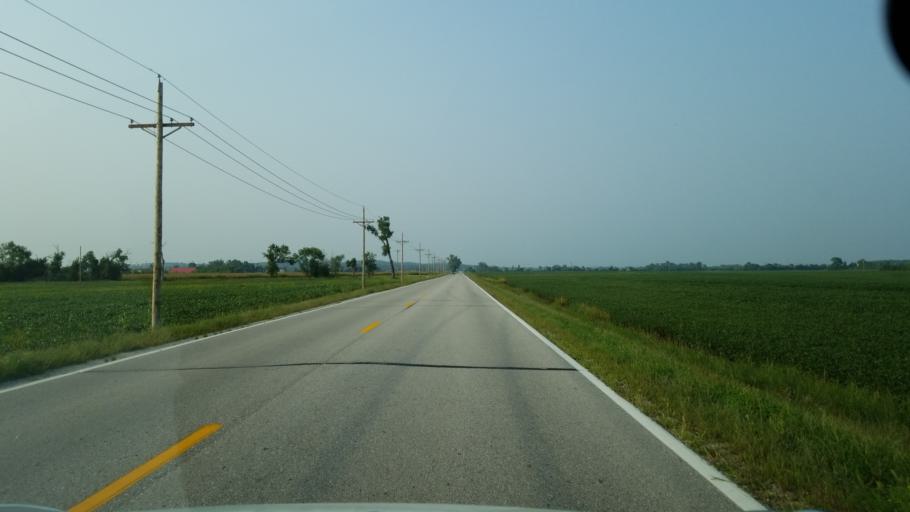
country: US
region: Nebraska
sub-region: Sarpy County
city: Offutt Air Force Base
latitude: 41.0950
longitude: -95.8898
